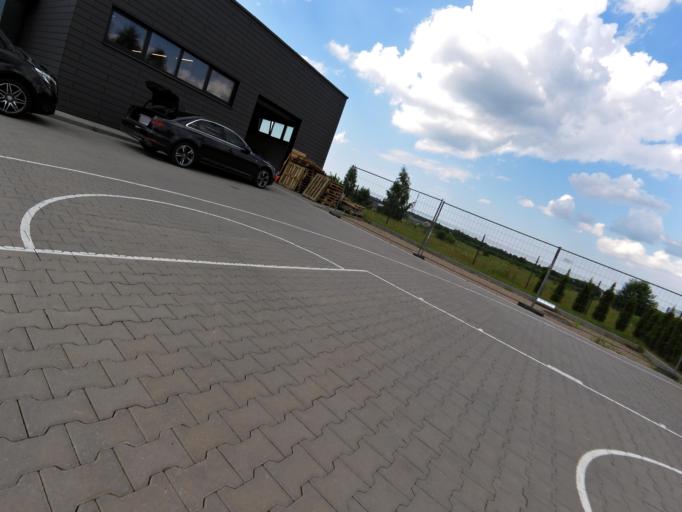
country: LT
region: Vilnius County
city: Pasilaiciai
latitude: 54.7517
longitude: 25.2186
